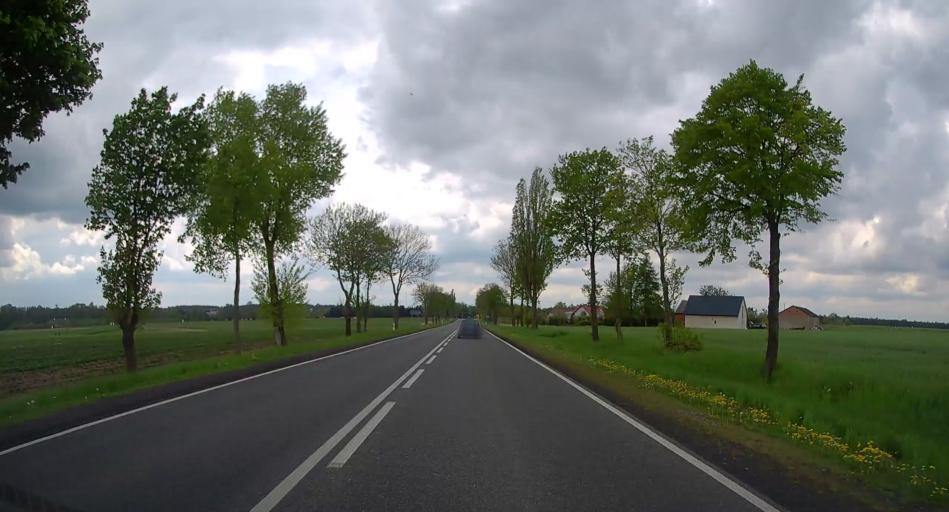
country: PL
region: Masovian Voivodeship
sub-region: Powiat plonski
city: Zaluski
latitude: 52.4360
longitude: 20.4742
